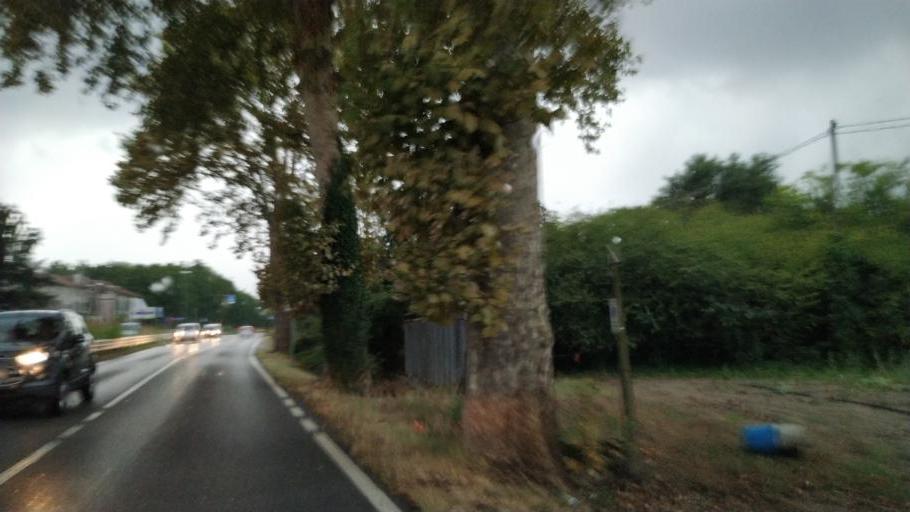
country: IT
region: Emilia-Romagna
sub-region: Provincia di Ferrara
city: Pontegradella
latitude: 44.8477
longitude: 11.6621
